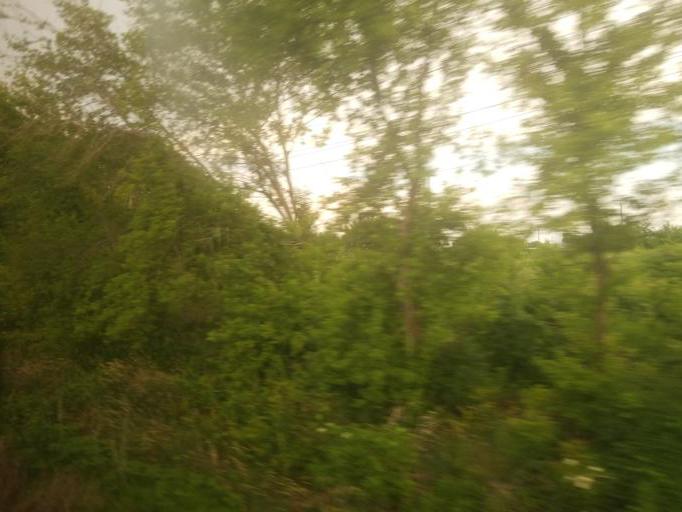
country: US
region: Illinois
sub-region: Bureau County
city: Princeton
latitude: 41.3889
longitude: -89.4558
